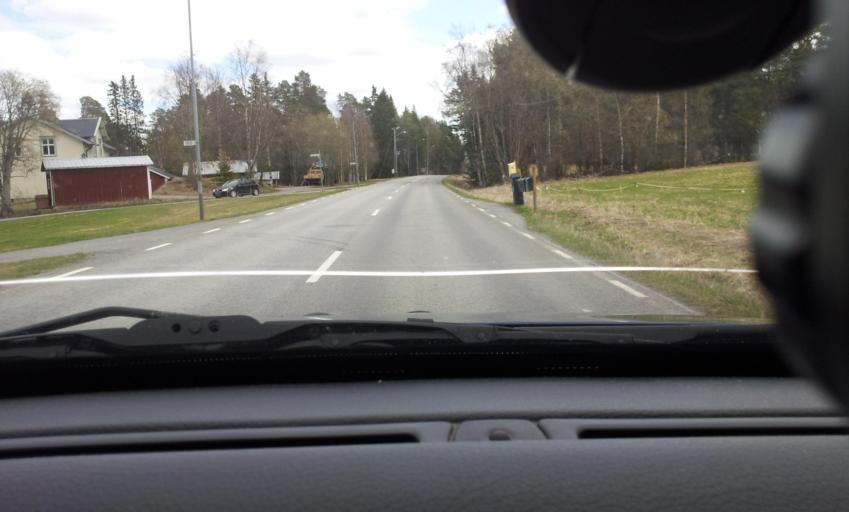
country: SE
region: Jaemtland
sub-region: OEstersunds Kommun
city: Ostersund
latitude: 63.1493
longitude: 14.6020
